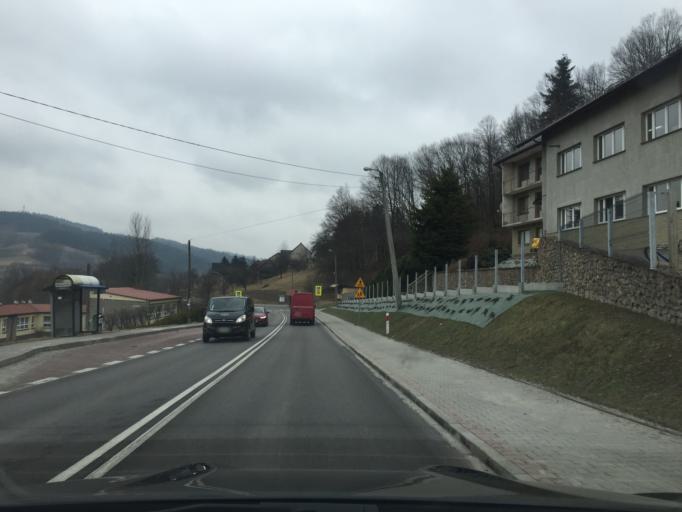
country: PL
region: Lesser Poland Voivodeship
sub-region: Powiat suski
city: Palcza
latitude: 49.7909
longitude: 19.7190
